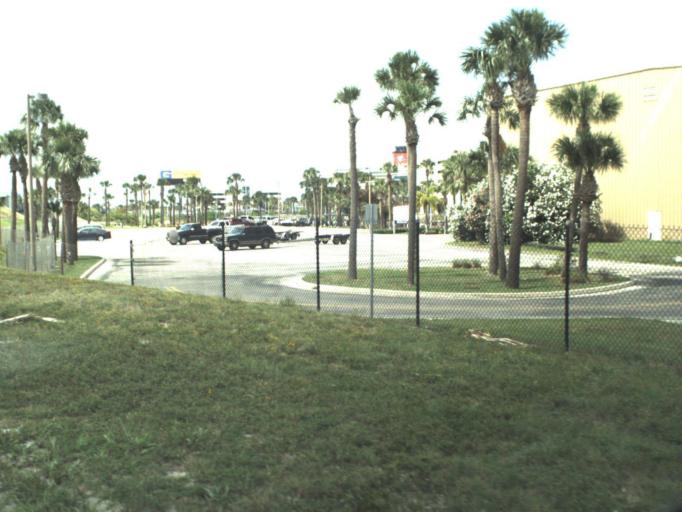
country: US
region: Florida
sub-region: Brevard County
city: Cape Canaveral
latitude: 28.4073
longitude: -80.6317
